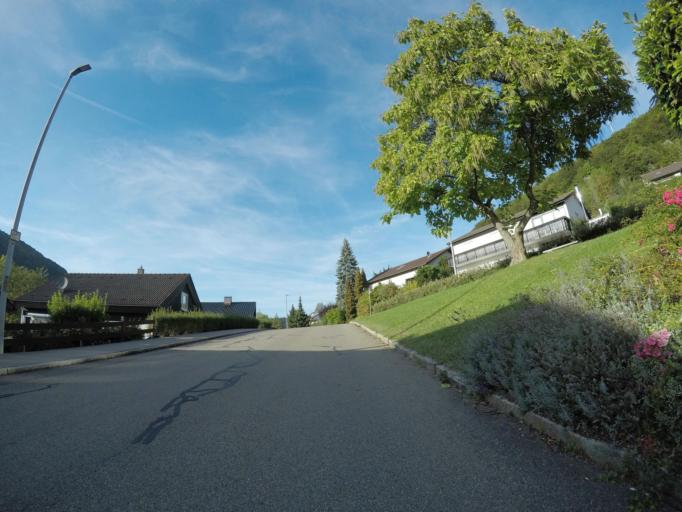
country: DE
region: Baden-Wuerttemberg
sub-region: Tuebingen Region
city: Pfullingen
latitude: 48.4287
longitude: 9.2589
